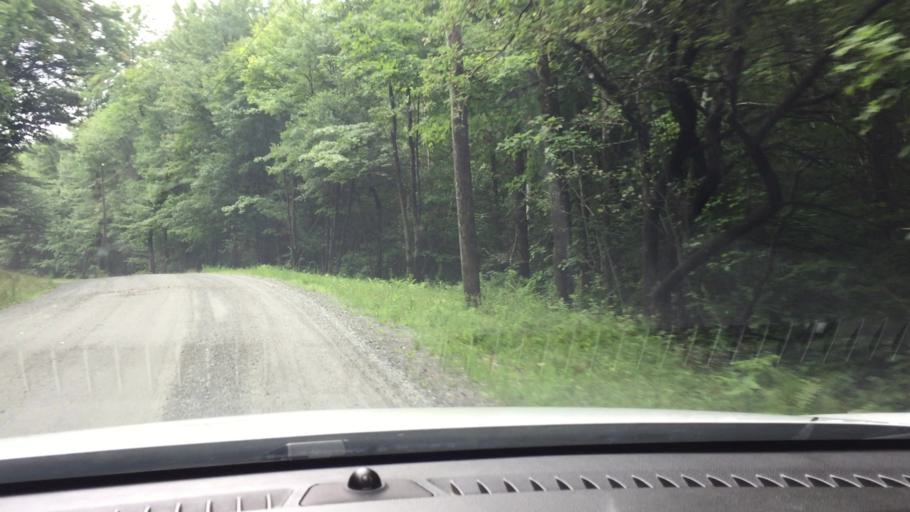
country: US
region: Massachusetts
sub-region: Berkshire County
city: Hinsdale
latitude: 42.4114
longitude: -73.0554
